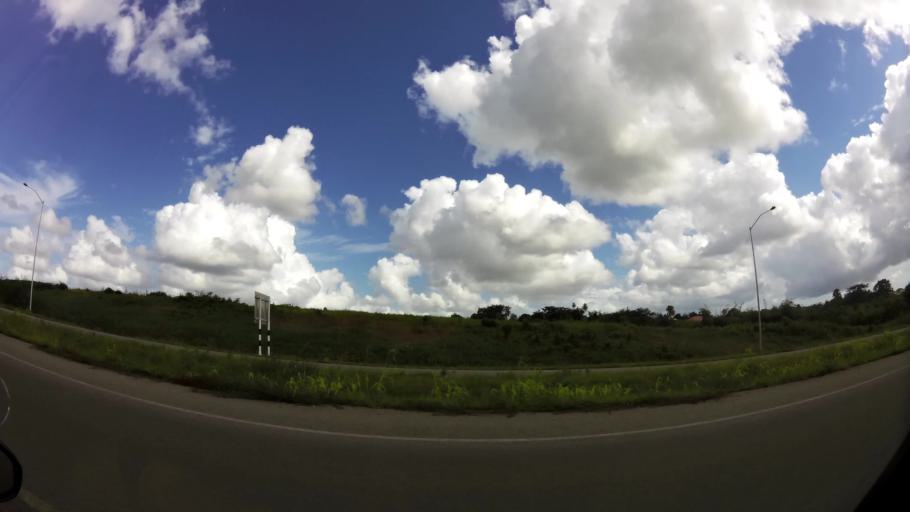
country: TT
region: Penal/Debe
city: Debe
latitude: 10.2386
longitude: -61.4462
